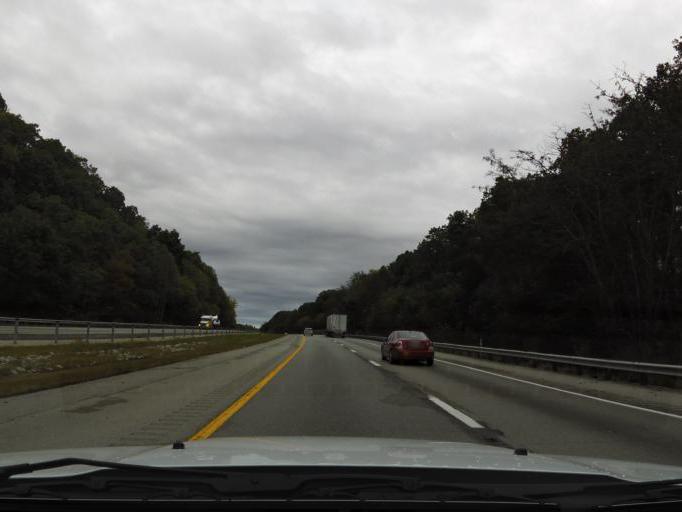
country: US
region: Kentucky
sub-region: Rockcastle County
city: Mount Vernon
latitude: 37.3006
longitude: -84.2792
